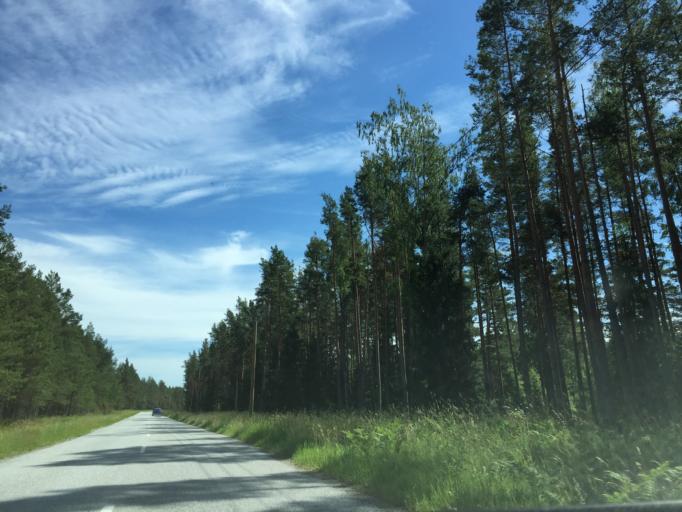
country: LV
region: Talsu Rajons
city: Valdemarpils
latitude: 57.5969
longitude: 22.6030
